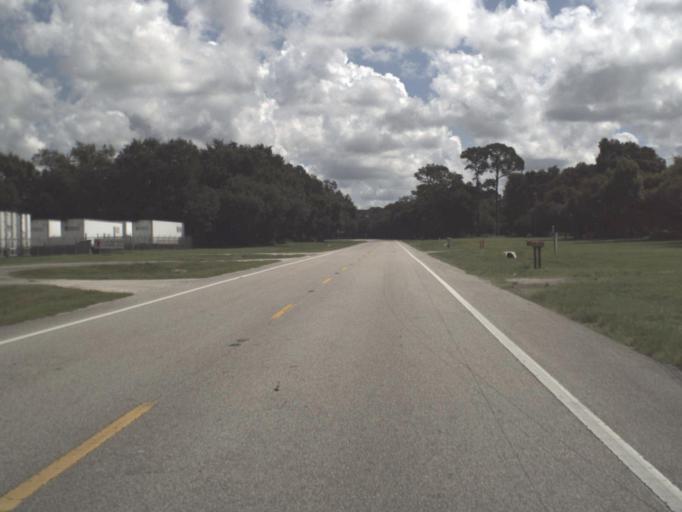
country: US
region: Florida
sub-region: Polk County
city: Polk City
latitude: 28.1524
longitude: -81.8718
